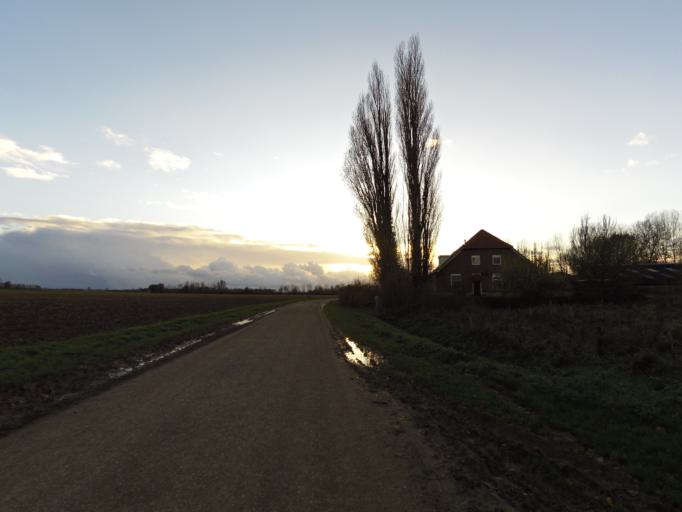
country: NL
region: Gelderland
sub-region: Oude IJsselstreek
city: Gendringen
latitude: 51.8695
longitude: 6.3432
